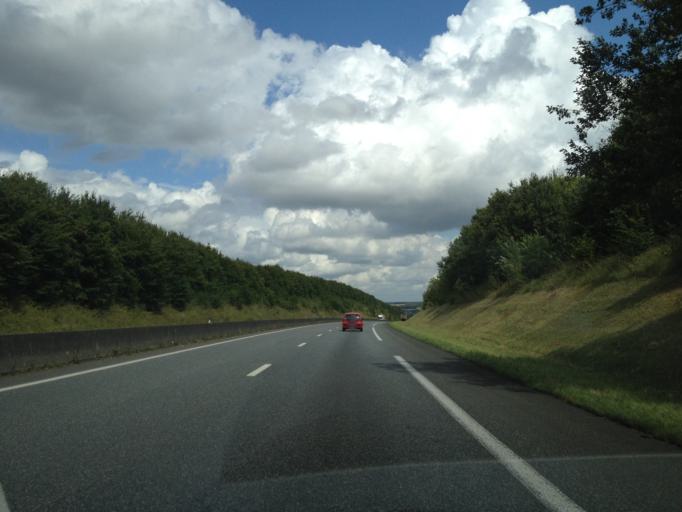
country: FR
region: Picardie
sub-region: Departement de la Somme
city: Abbeville
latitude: 50.0954
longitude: 1.7778
